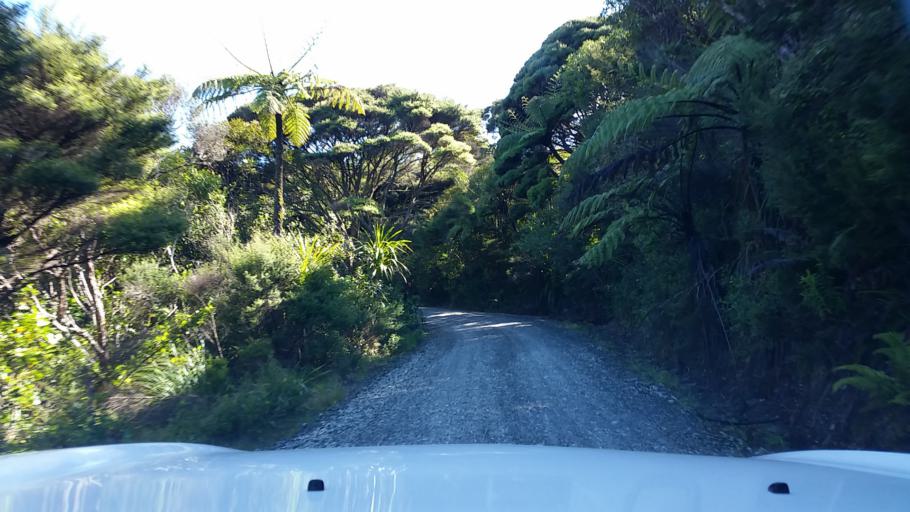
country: NZ
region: Auckland
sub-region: Auckland
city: Titirangi
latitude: -37.0173
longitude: 174.5372
